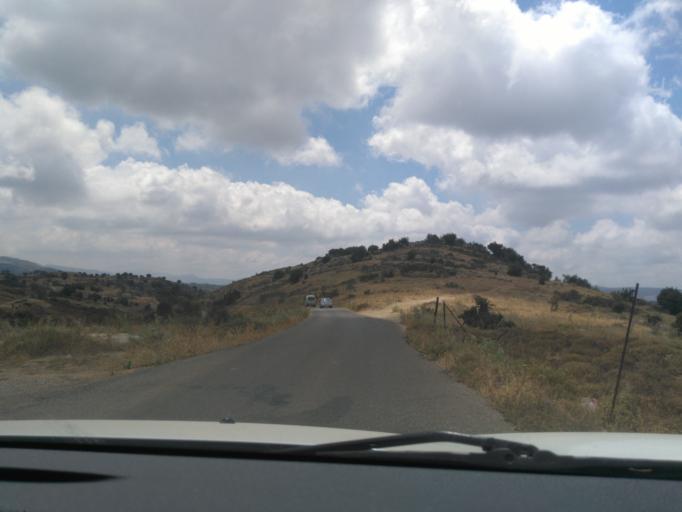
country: LB
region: Mont-Liban
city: Beit ed Dine
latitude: 33.6847
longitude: 35.6654
